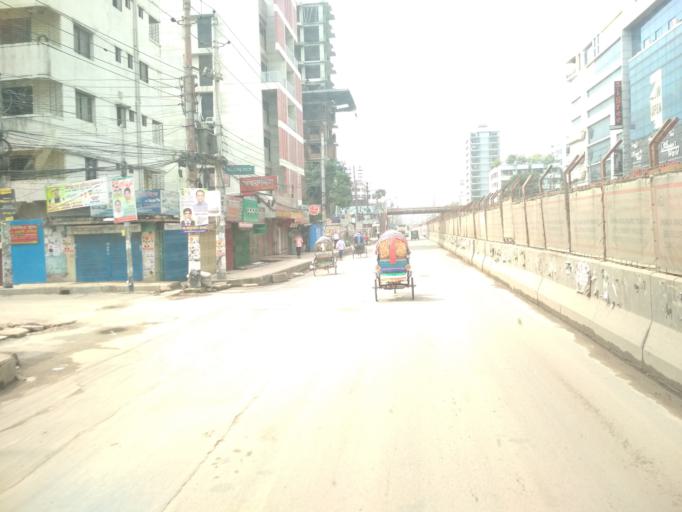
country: BD
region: Dhaka
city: Tungi
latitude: 23.8155
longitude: 90.3664
